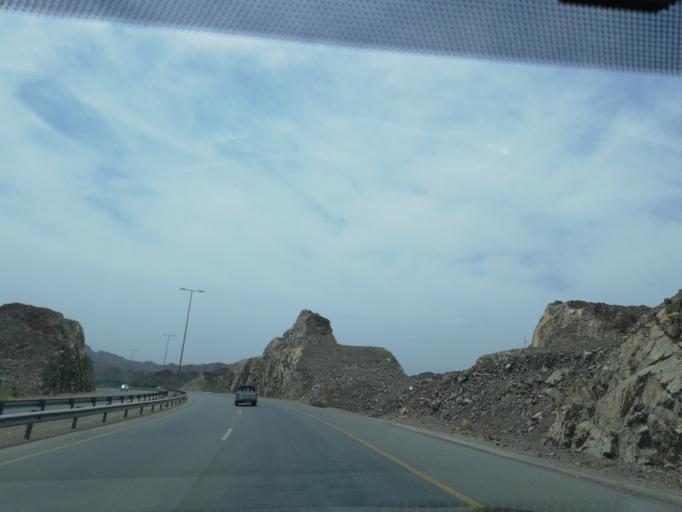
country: OM
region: Muhafazat ad Dakhiliyah
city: Sufalat Sama'il
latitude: 23.3630
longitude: 58.0330
